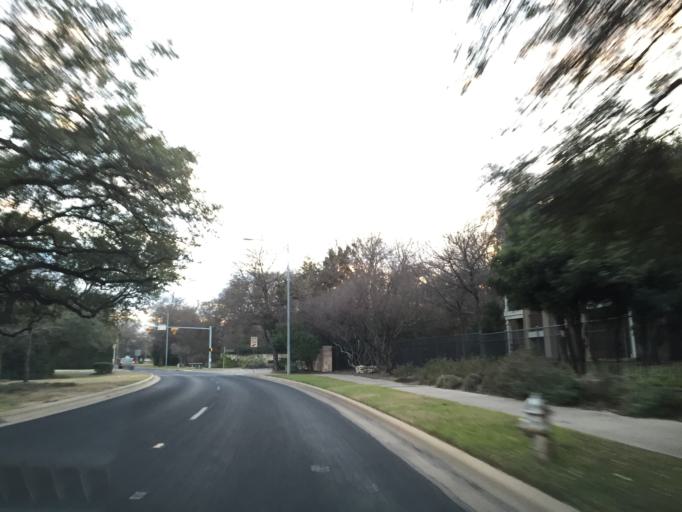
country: US
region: Texas
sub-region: Williamson County
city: Jollyville
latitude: 30.4302
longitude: -97.7408
